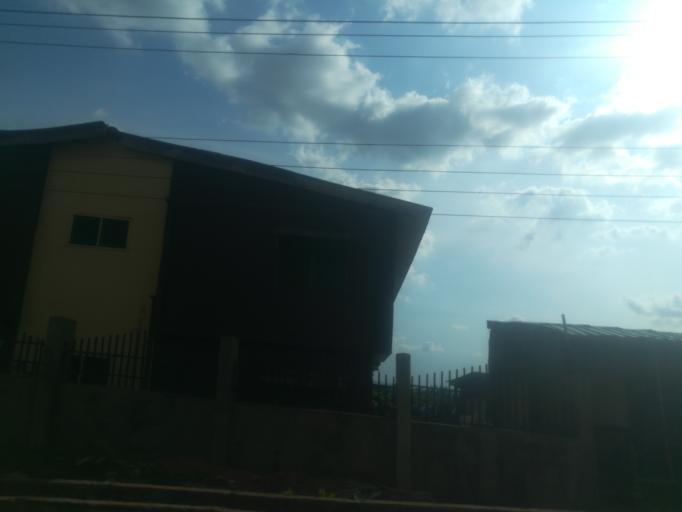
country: NG
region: Oyo
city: Ibadan
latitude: 7.4205
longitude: 3.8451
